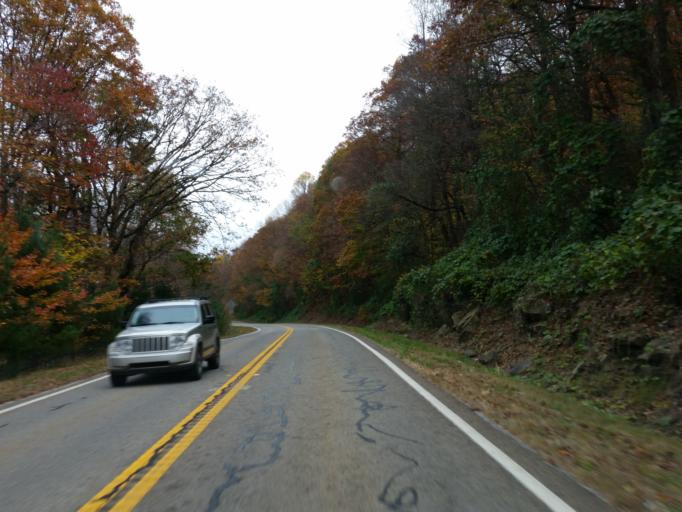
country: US
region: Georgia
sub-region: Pickens County
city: Jasper
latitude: 34.5446
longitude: -84.3627
